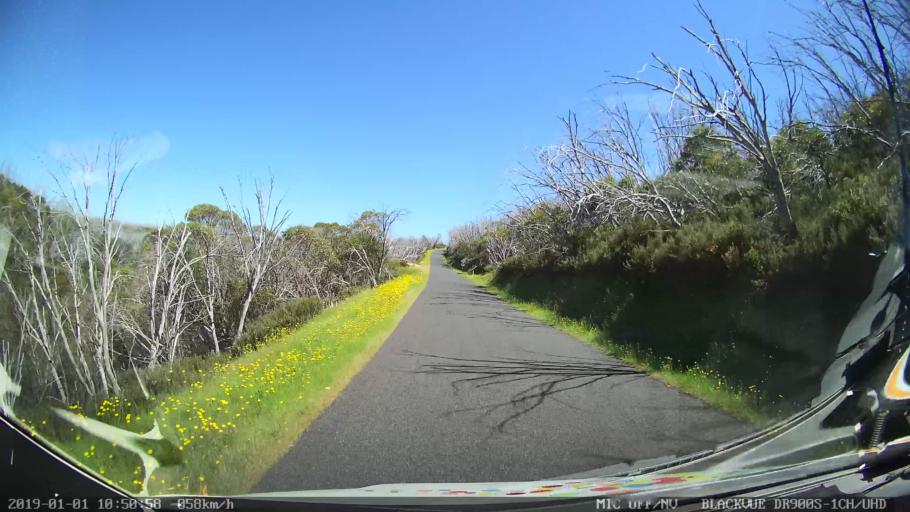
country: AU
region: New South Wales
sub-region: Snowy River
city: Jindabyne
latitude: -36.0235
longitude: 148.3721
